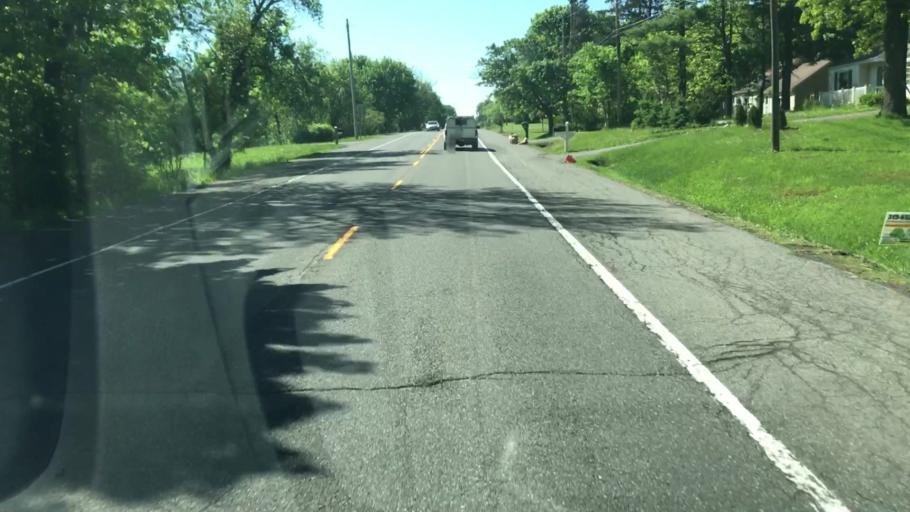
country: US
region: New York
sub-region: Onondaga County
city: Seneca Knolls
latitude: 43.1342
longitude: -76.2598
